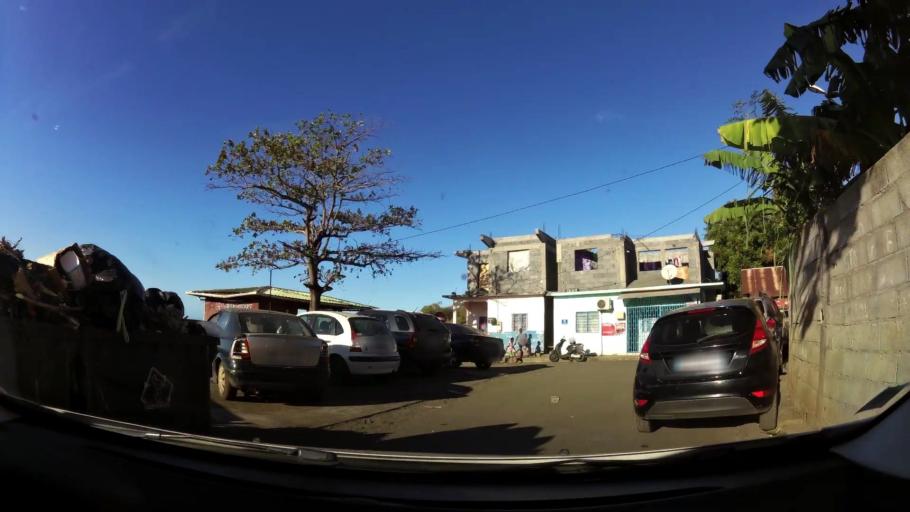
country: YT
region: Koungou
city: Koungou
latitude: -12.7351
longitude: 45.2078
